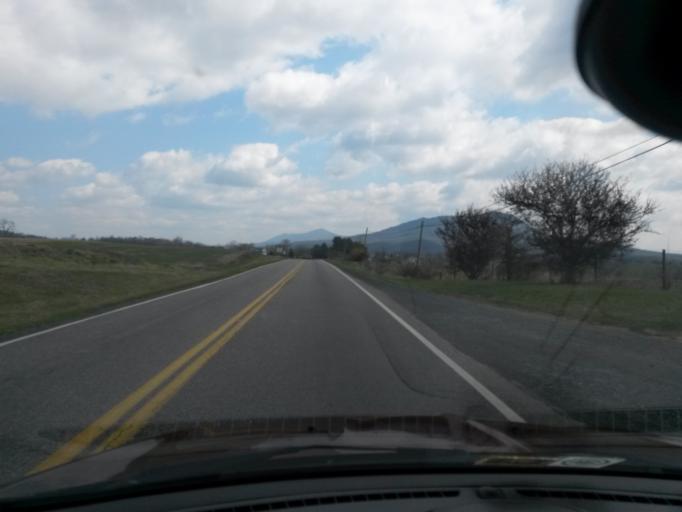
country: US
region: Virginia
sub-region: Rockingham County
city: Massanetta Springs
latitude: 38.3677
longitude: -78.8317
